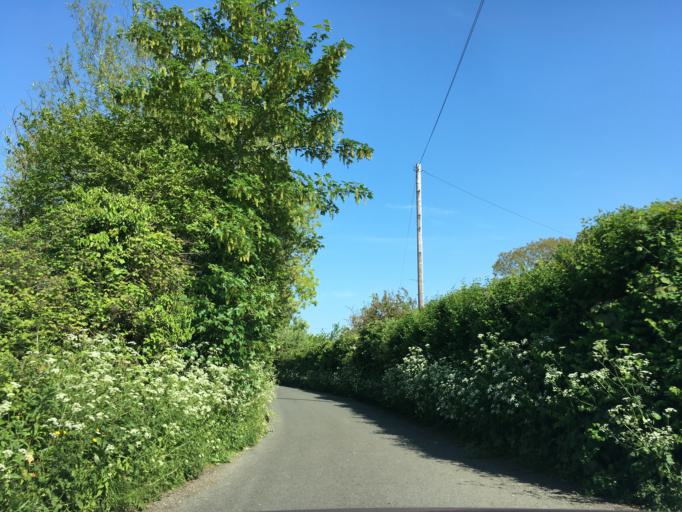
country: GB
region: England
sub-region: Gloucestershire
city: Stonehouse
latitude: 51.7460
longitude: -2.3214
